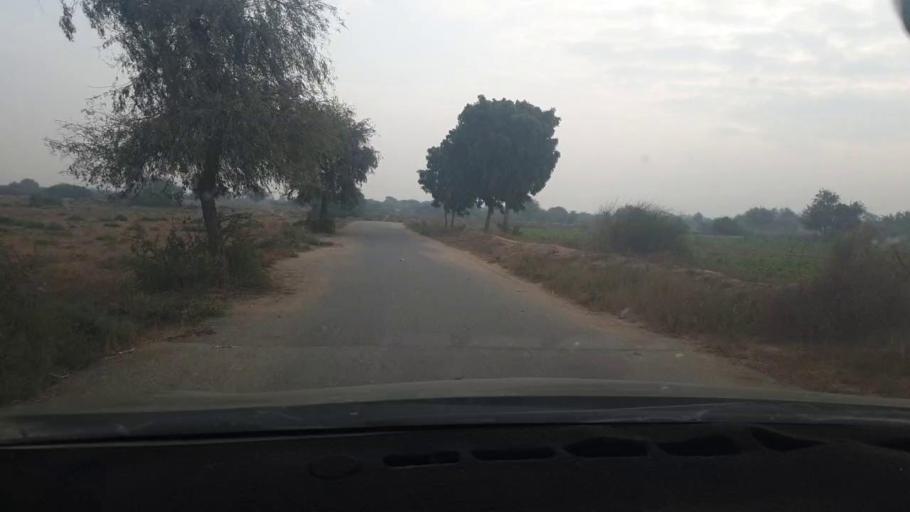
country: PK
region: Sindh
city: Malir Cantonment
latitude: 24.9580
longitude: 67.4064
